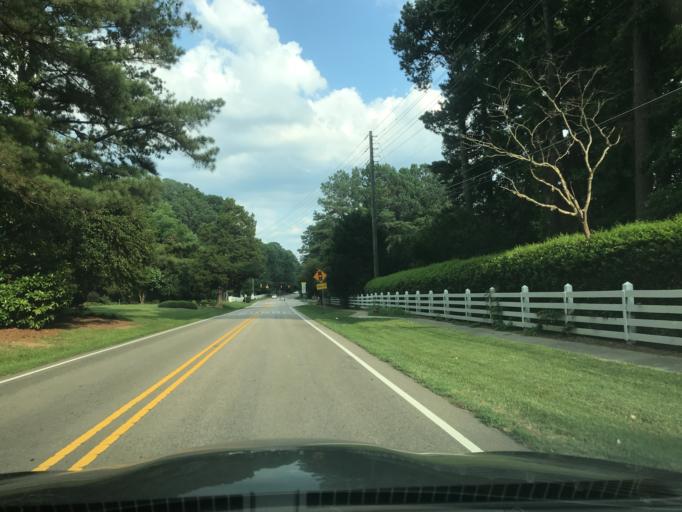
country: US
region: North Carolina
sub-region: Wake County
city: Cary
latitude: 35.8943
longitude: -78.7188
